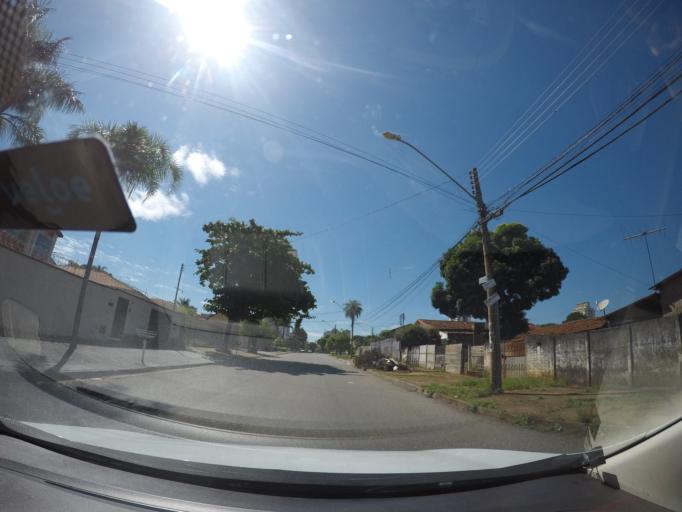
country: BR
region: Goias
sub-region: Goiania
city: Goiania
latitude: -16.6989
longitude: -49.2887
